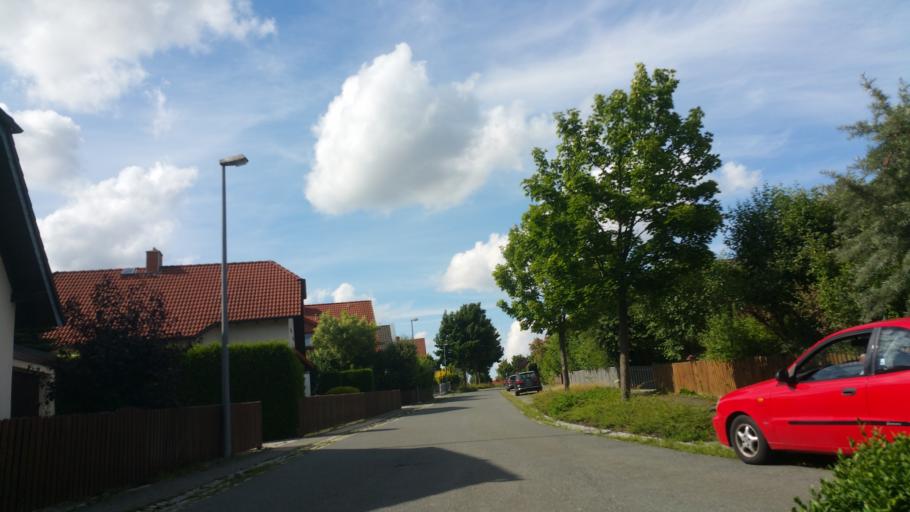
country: DE
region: Bavaria
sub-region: Upper Franconia
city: Oberkotzau
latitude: 50.2538
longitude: 11.9285
